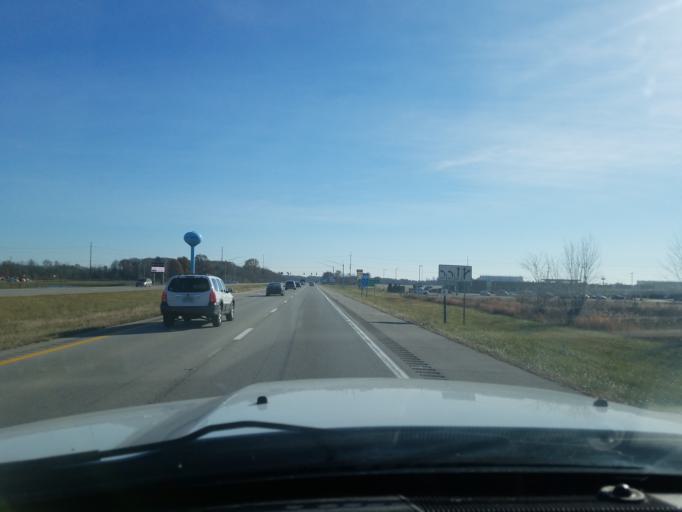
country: US
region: Ohio
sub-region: Brown County
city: Mount Orab
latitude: 39.0469
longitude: -83.9433
